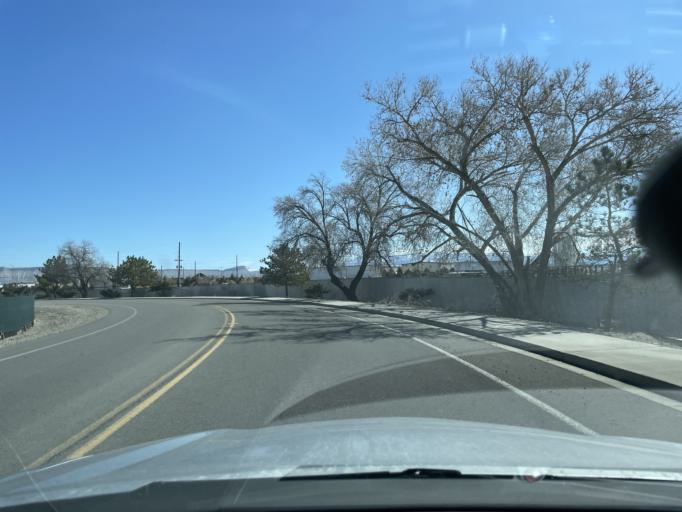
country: US
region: Colorado
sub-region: Mesa County
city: Redlands
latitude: 39.0890
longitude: -108.6096
